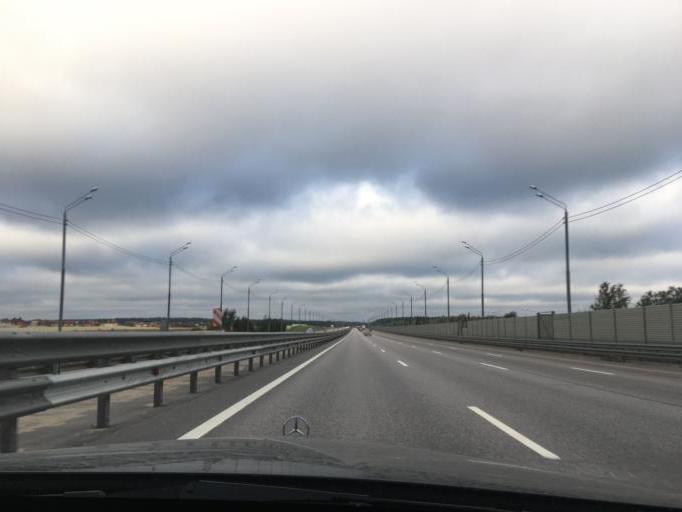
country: RU
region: Moskovskaya
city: Rozhdestveno
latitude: 55.8190
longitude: 36.9910
